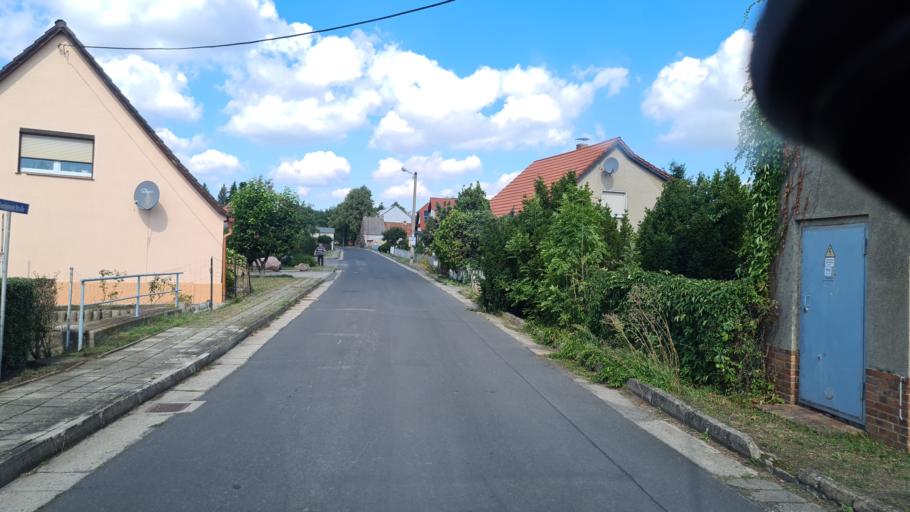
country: DE
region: Brandenburg
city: Spremberg
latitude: 51.6513
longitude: 14.3332
